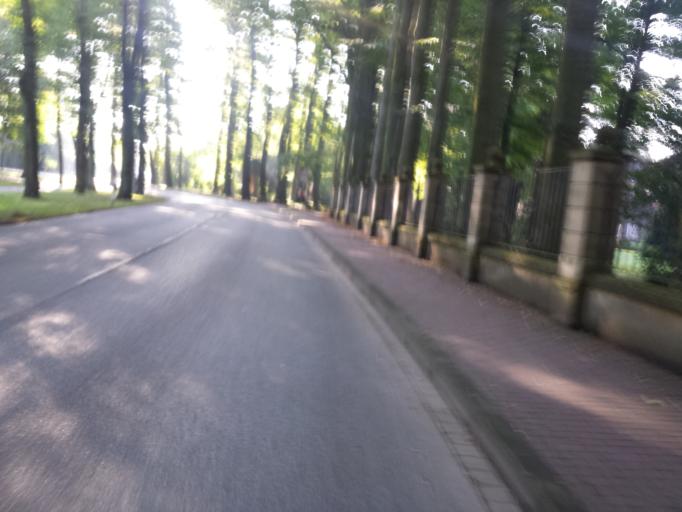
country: DE
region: North Rhine-Westphalia
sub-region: Regierungsbezirk Detmold
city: Harsewinkel
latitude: 51.9478
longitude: 8.2793
